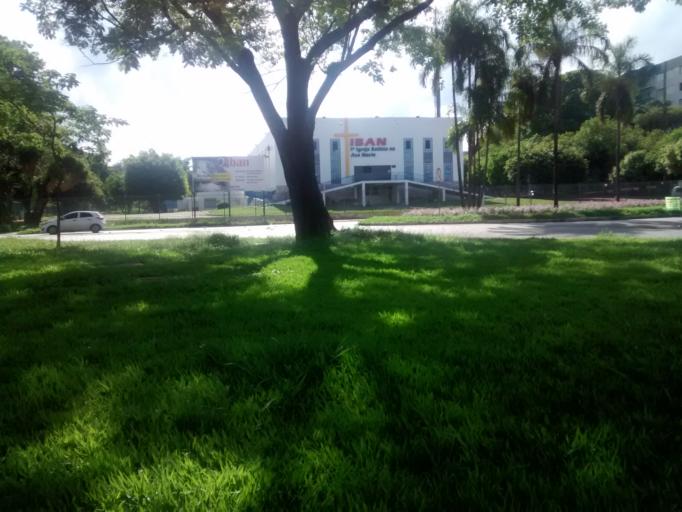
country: BR
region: Federal District
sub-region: Brasilia
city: Brasilia
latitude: -15.7469
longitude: -47.8924
